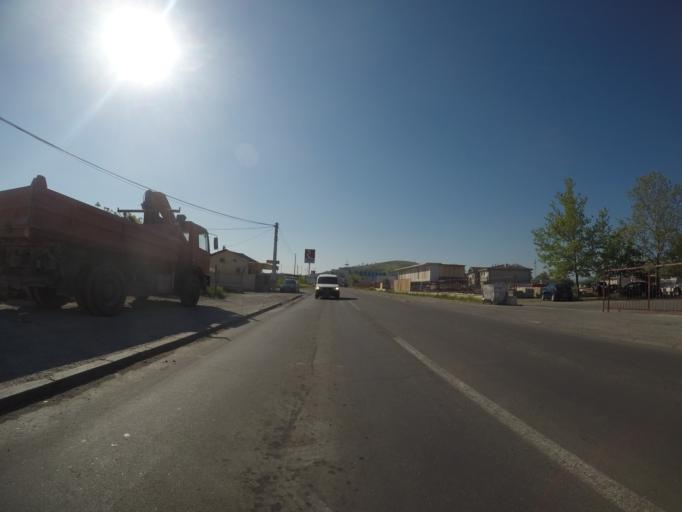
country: ME
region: Podgorica
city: Podgorica
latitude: 42.4314
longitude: 19.2307
